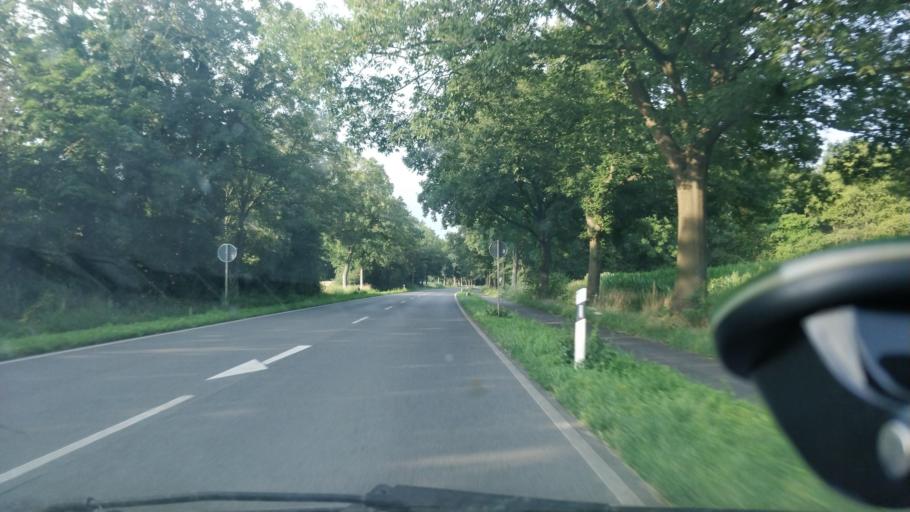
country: DE
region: North Rhine-Westphalia
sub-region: Regierungsbezirk Dusseldorf
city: Kamp-Lintfort
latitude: 51.4970
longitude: 6.5096
